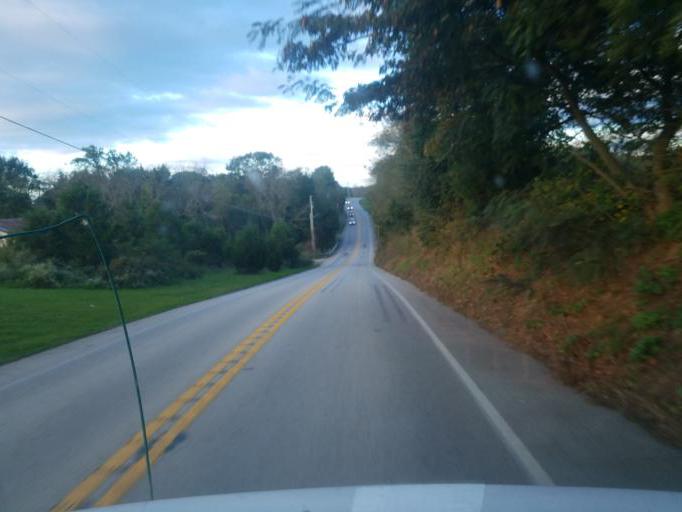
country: US
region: Pennsylvania
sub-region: York County
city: Spring Grove
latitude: 39.9394
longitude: -76.8965
